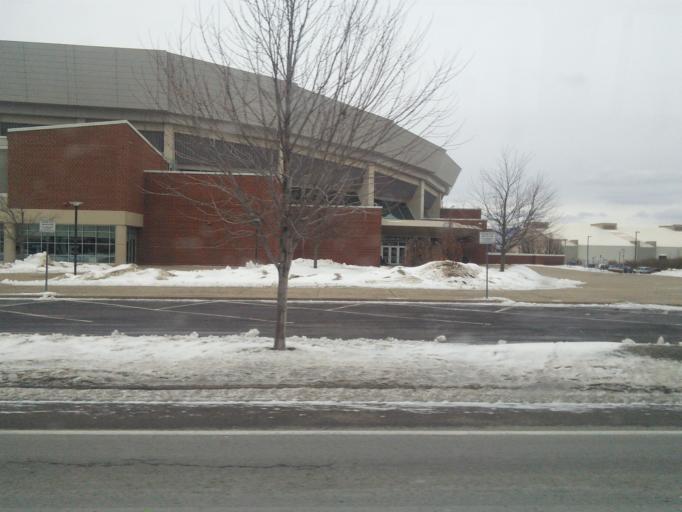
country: US
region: Pennsylvania
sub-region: Centre County
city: State College
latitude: 40.8090
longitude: -77.8571
